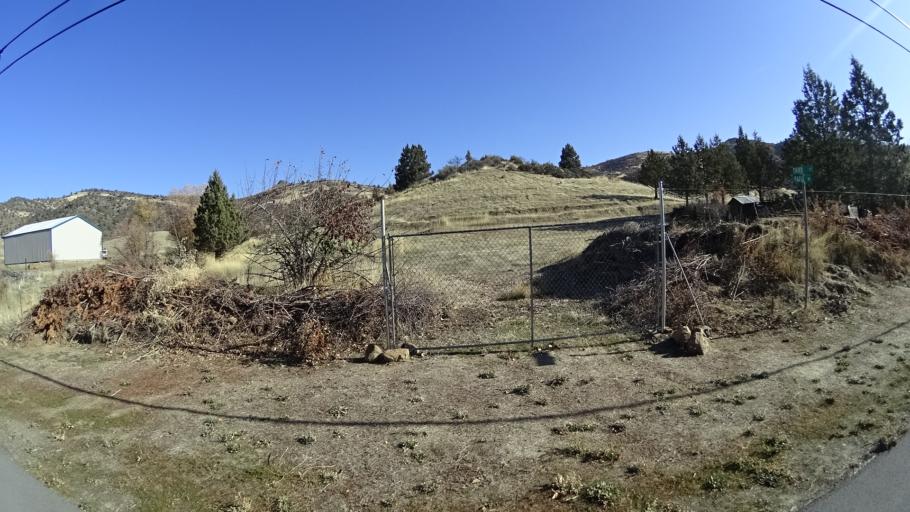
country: US
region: California
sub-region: Siskiyou County
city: Montague
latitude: 41.9133
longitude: -122.5567
